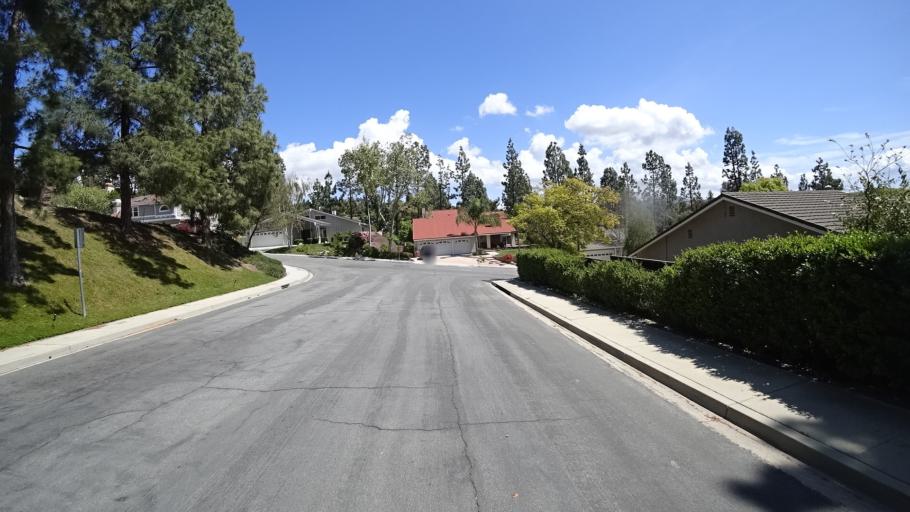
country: US
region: California
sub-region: Ventura County
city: Thousand Oaks
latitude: 34.2205
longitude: -118.8427
